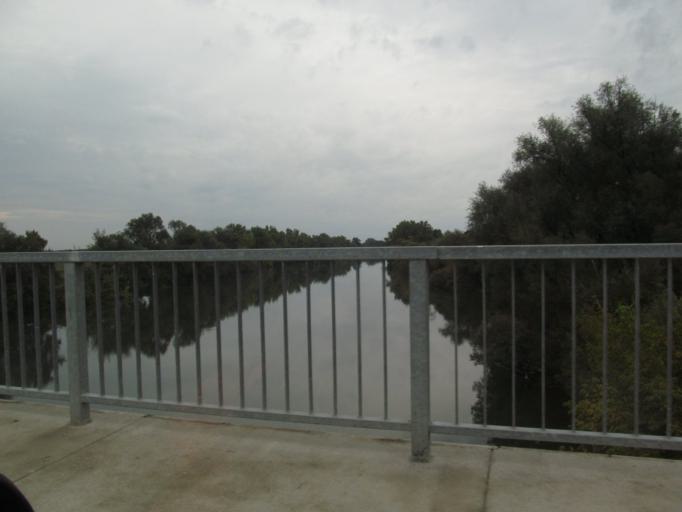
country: HR
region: Zagrebacka
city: Jastrebarsko
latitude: 45.5101
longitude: 15.7262
